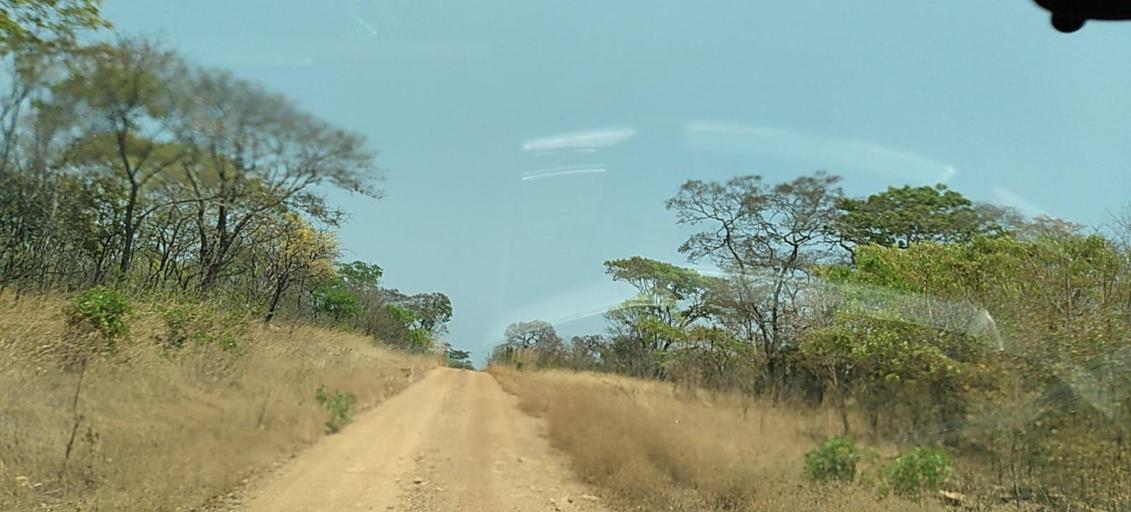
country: ZM
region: Central
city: Mumbwa
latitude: -14.4177
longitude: 26.4888
